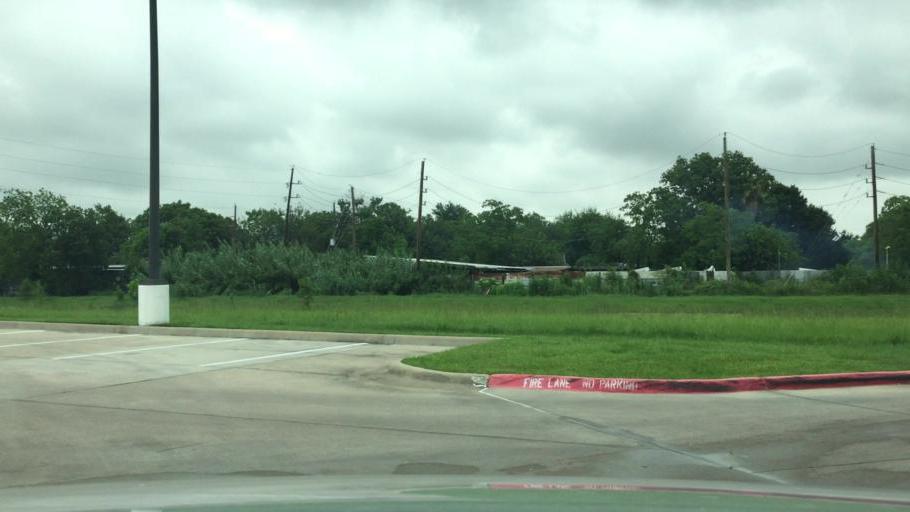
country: US
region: Texas
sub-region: Harris County
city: Jersey Village
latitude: 29.9046
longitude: -95.5511
